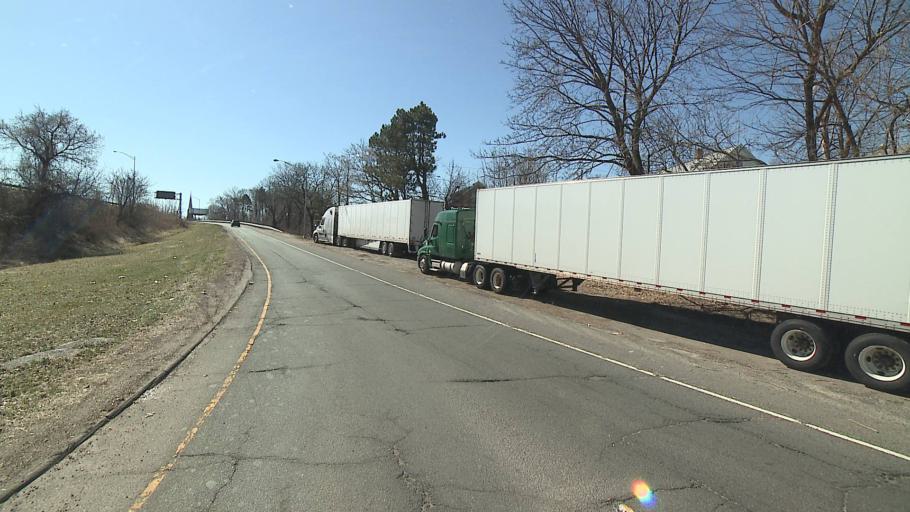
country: US
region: Connecticut
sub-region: Fairfield County
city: Bridgeport
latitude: 41.1975
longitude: -73.1953
